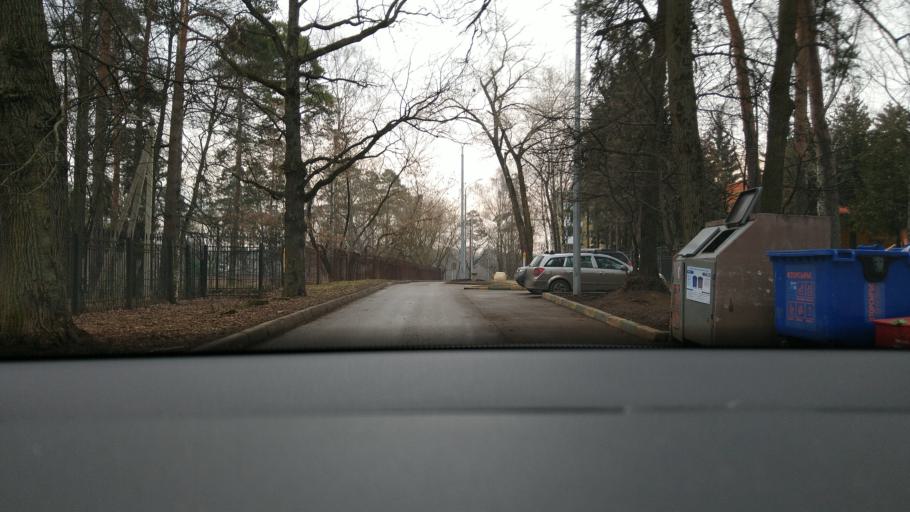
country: RU
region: Moscow
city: Novo-Peredelkino
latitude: 55.6589
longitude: 37.3496
